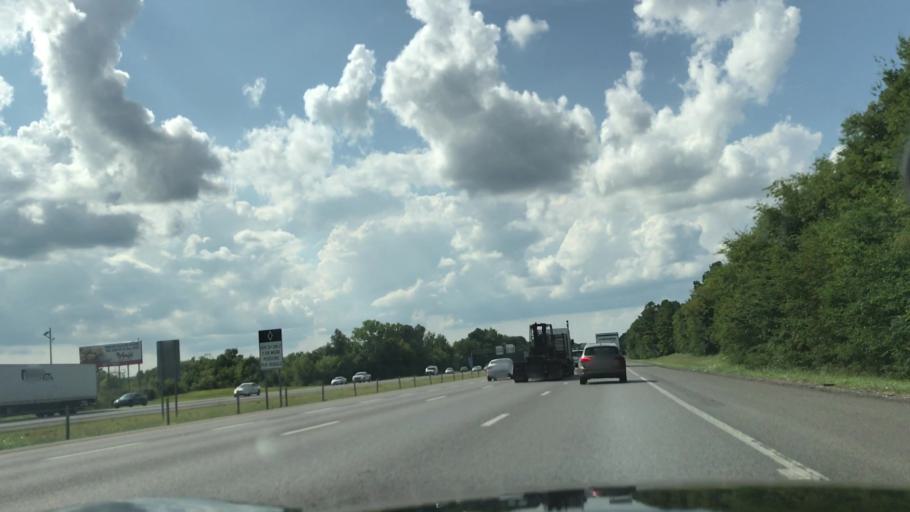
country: US
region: Tennessee
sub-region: Rutherford County
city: Smyrna
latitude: 35.8920
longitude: -86.4842
